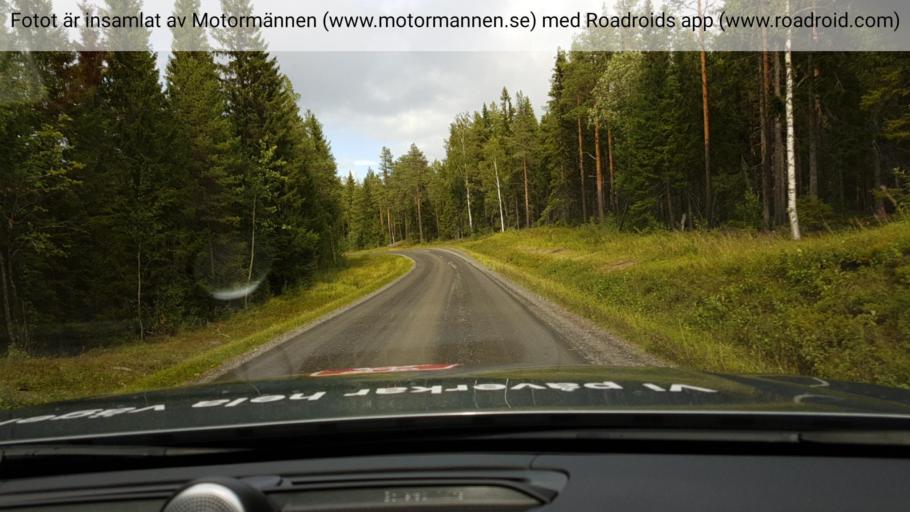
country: SE
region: Jaemtland
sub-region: OEstersunds Kommun
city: Lit
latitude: 63.7476
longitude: 14.6523
